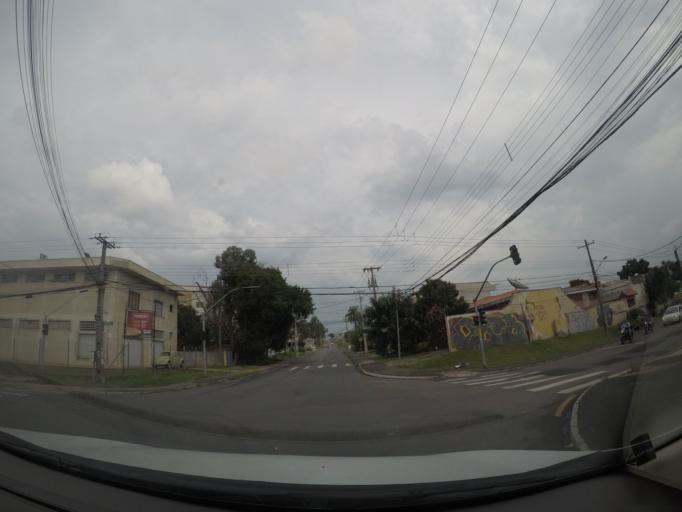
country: BR
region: Parana
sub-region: Sao Jose Dos Pinhais
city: Sao Jose dos Pinhais
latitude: -25.5215
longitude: -49.2612
